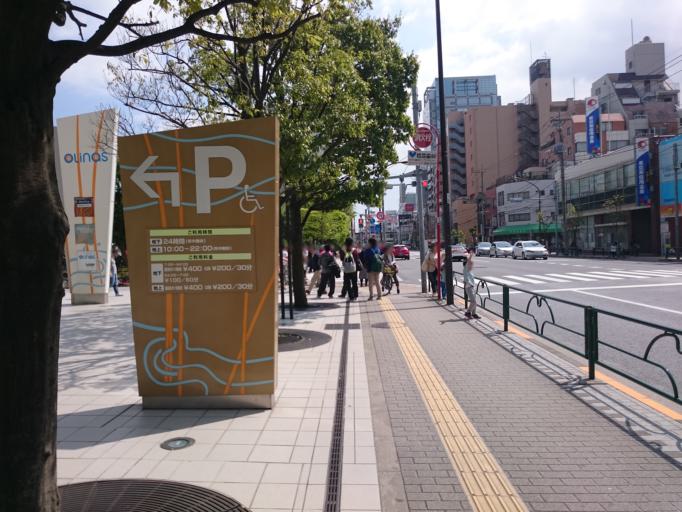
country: JP
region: Tokyo
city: Urayasu
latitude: 35.7002
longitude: 139.8149
